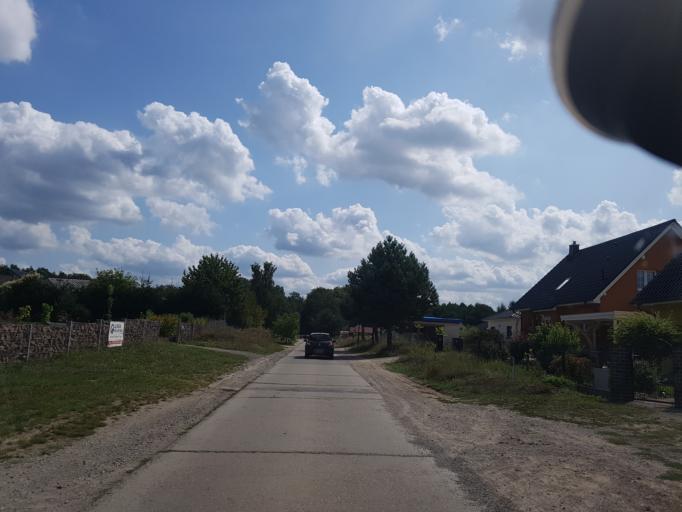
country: DE
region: Brandenburg
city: Gross Kreutz
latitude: 52.3182
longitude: 12.7674
